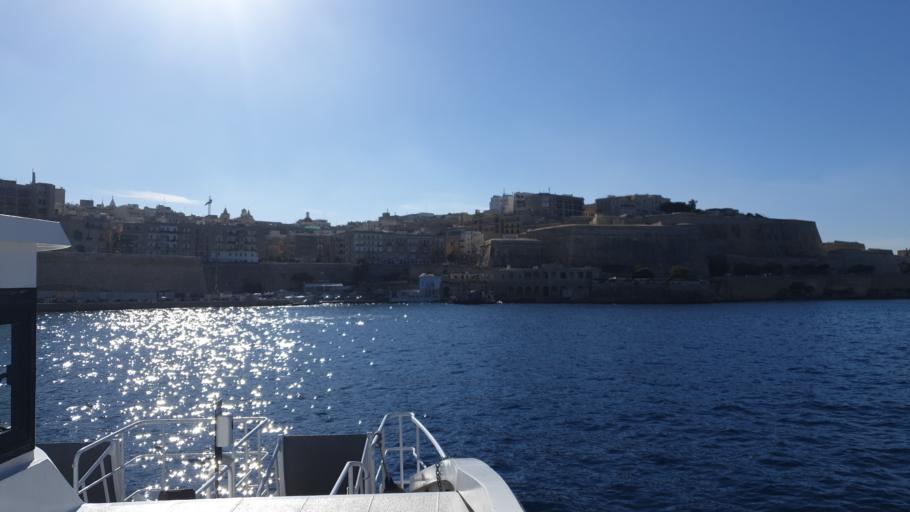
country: MT
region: Il-Belt Valletta
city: Valletta
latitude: 35.9029
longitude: 14.5095
